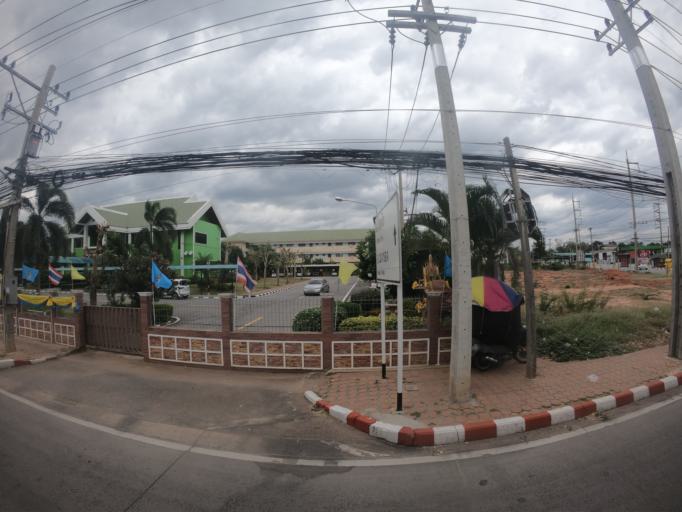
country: TH
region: Nakhon Ratchasima
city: Nakhon Ratchasima
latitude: 14.9157
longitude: 102.1490
